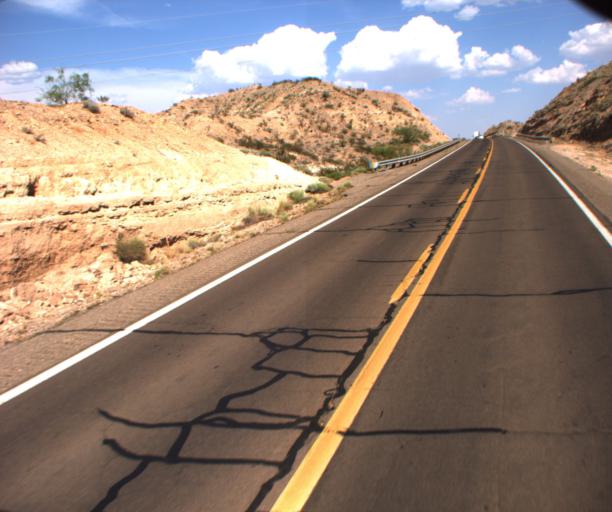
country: US
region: Arizona
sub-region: Greenlee County
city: Clifton
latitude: 32.7568
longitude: -109.1336
